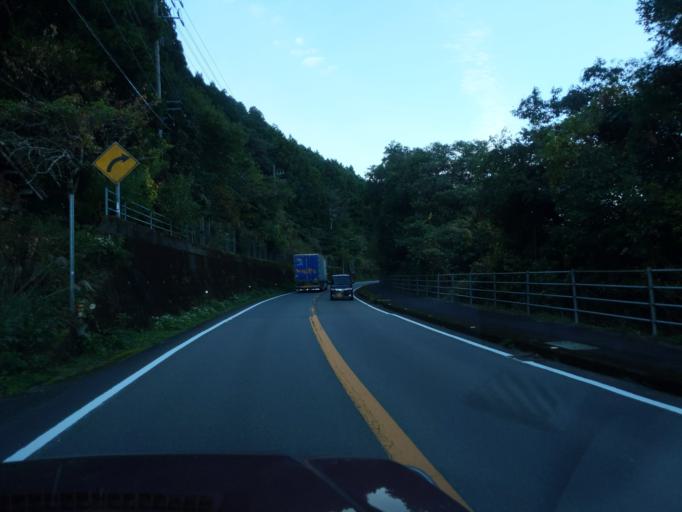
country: JP
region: Tokushima
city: Anan
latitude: 33.6879
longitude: 134.4255
